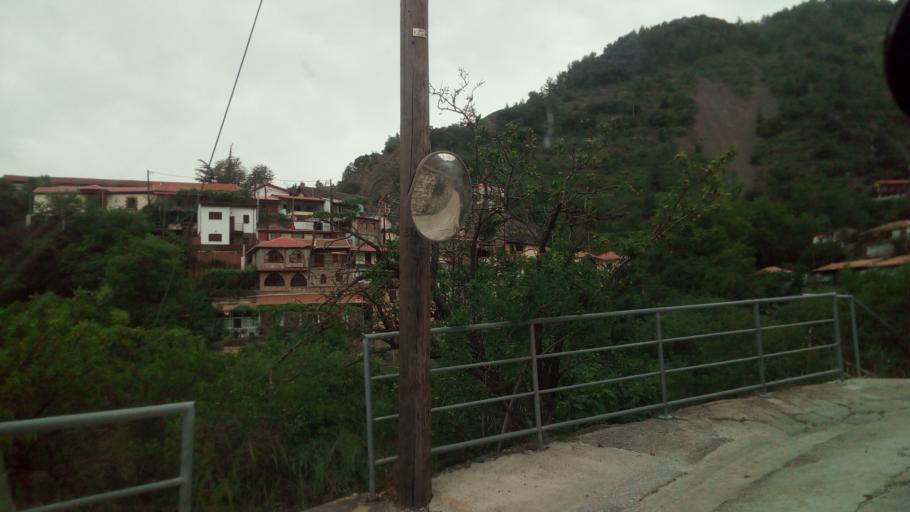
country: CY
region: Lefkosia
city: Kakopetria
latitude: 34.9624
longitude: 32.7523
